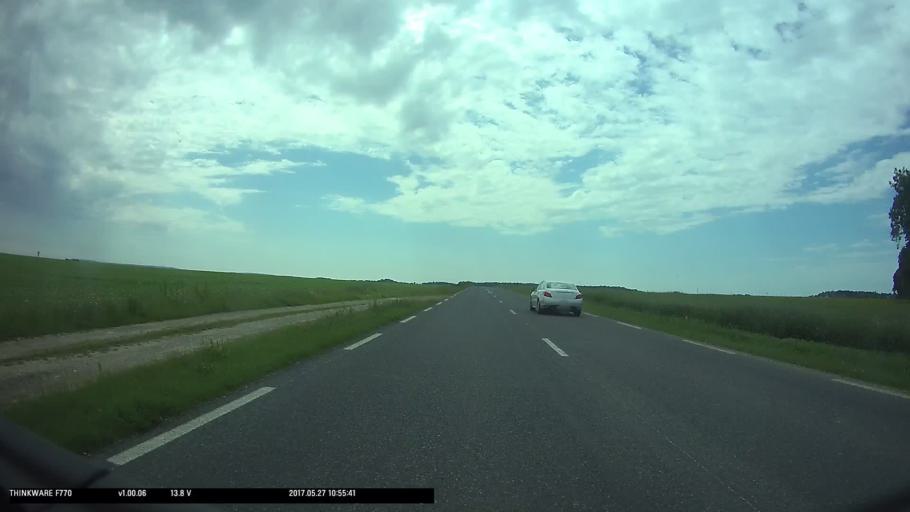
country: FR
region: Picardie
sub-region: Departement de l'Oise
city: Chaumont-en-Vexin
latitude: 49.2323
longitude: 1.8806
